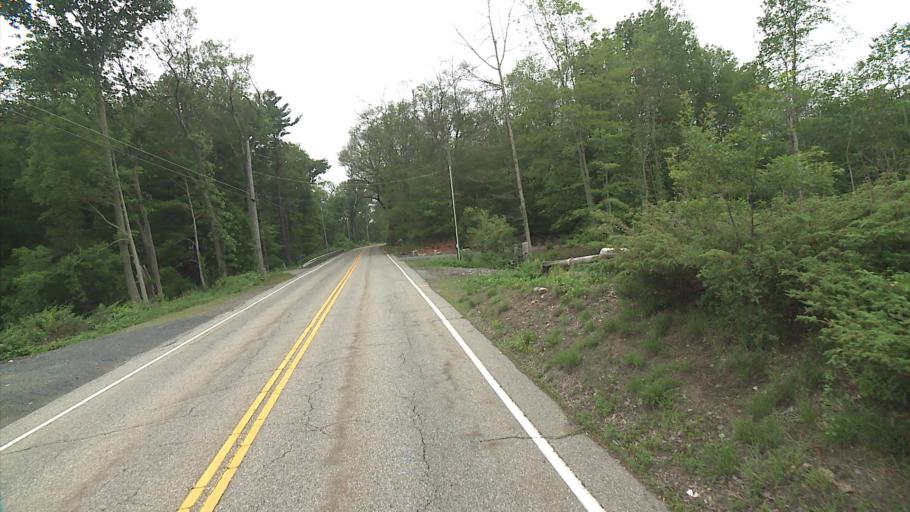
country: US
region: Connecticut
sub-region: Tolland County
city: Hebron
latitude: 41.7055
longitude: -72.3652
